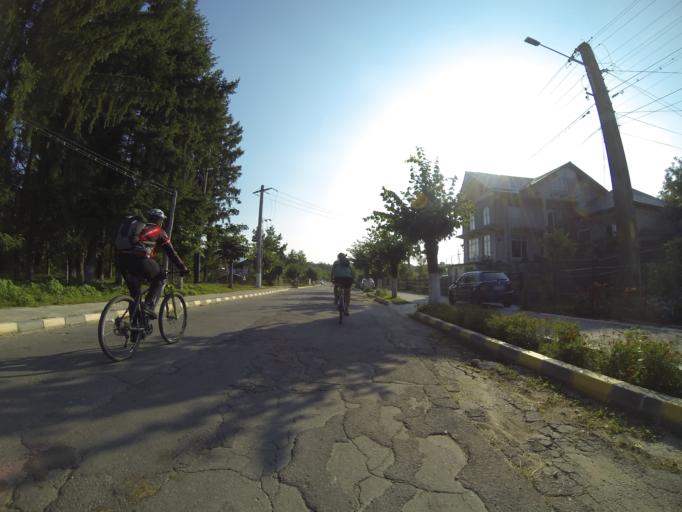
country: RO
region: Valcea
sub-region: Comuna Horezu
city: Horezu
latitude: 45.1480
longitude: 23.9967
